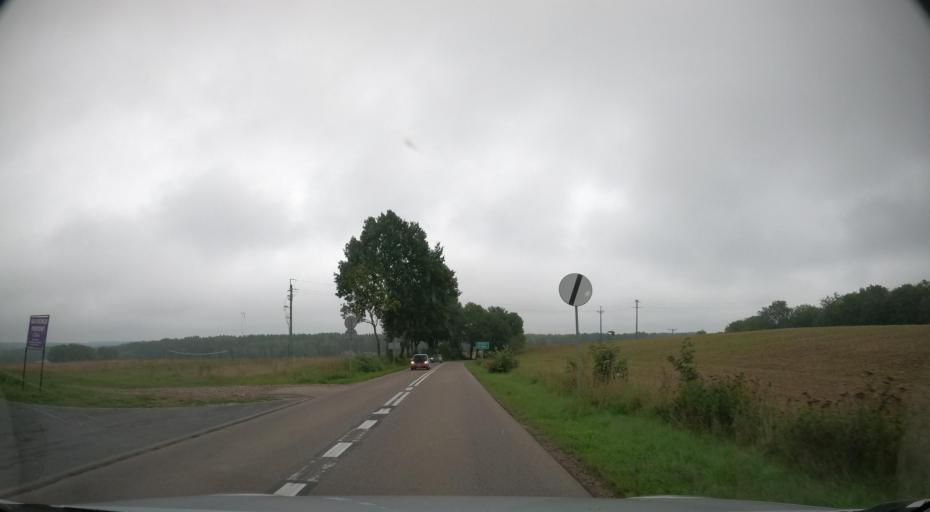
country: PL
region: Pomeranian Voivodeship
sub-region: Powiat wejherowski
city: Linia
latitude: 54.4581
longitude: 18.0385
